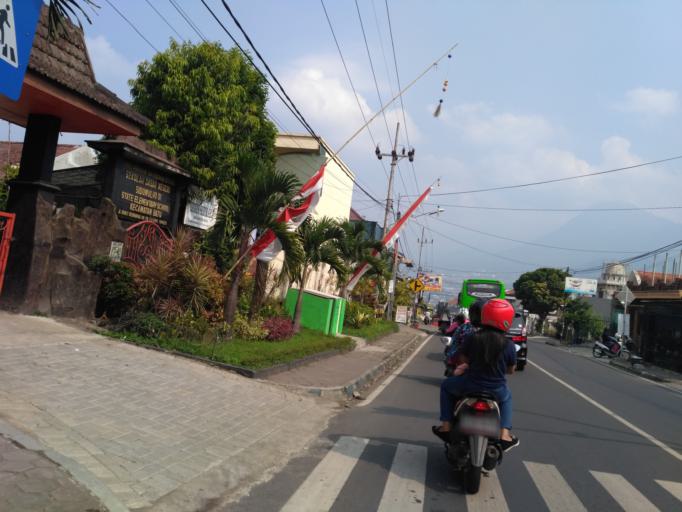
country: ID
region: East Java
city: Batu
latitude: -7.8506
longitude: 112.5281
